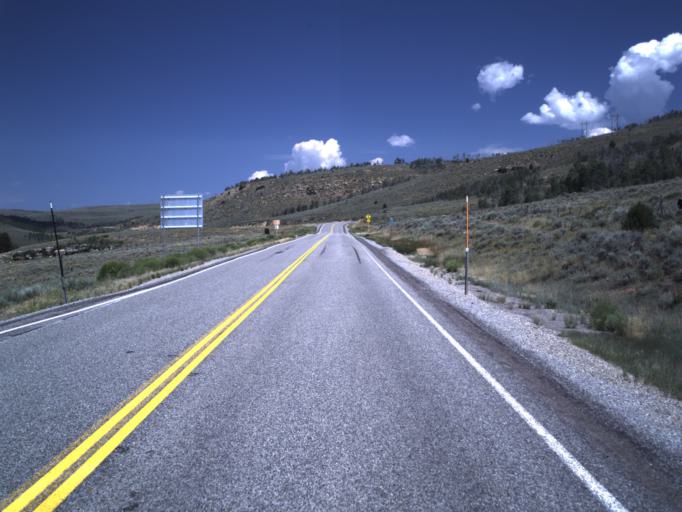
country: US
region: Utah
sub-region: Carbon County
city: Helper
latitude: 39.8174
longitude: -111.1353
